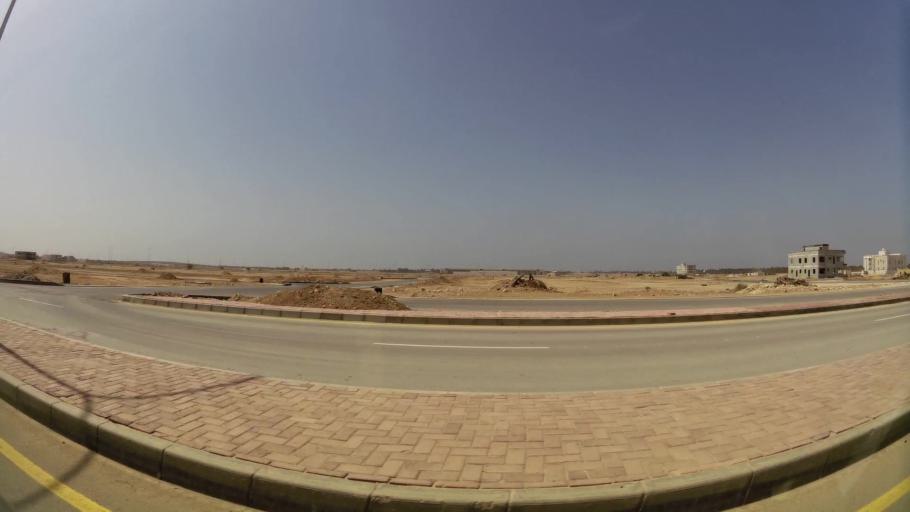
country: OM
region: Zufar
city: Salalah
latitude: 17.0404
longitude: 54.1252
